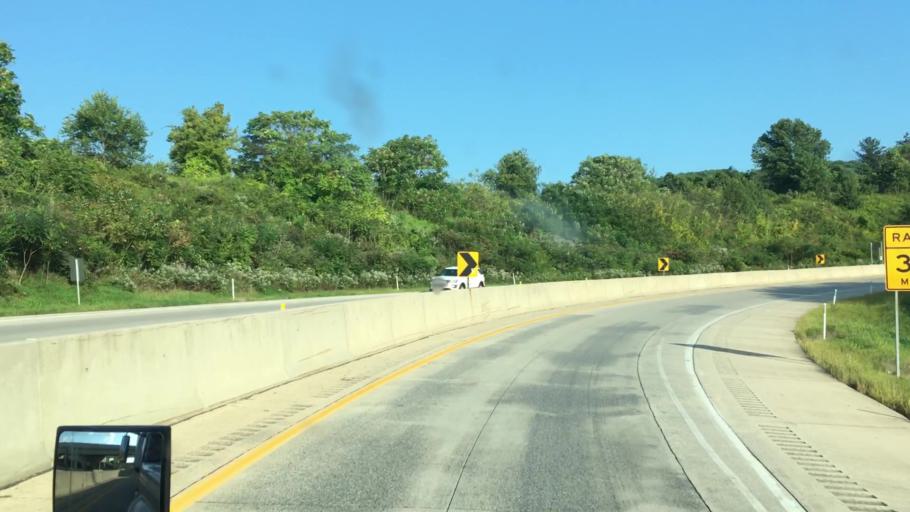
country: US
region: Pennsylvania
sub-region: Northampton County
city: Old Orchard
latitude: 40.6386
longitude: -75.2714
